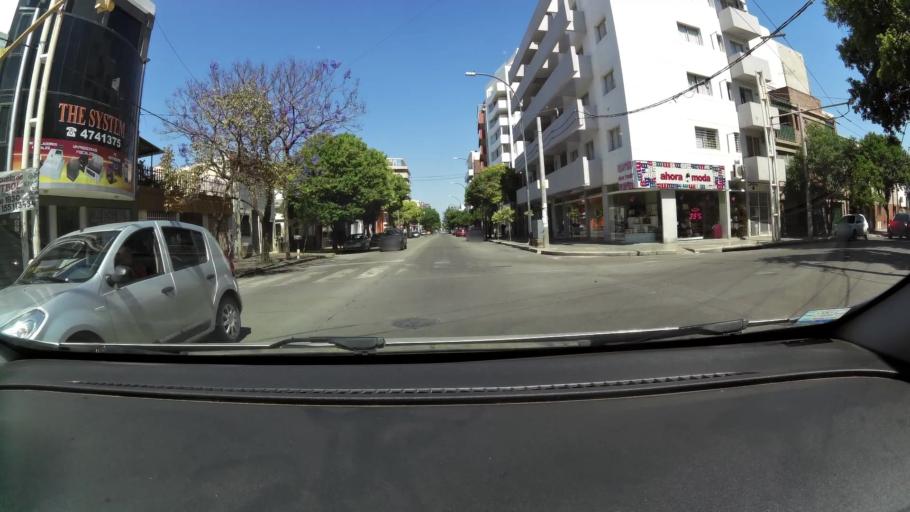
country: AR
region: Cordoba
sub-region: Departamento de Capital
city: Cordoba
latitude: -31.3903
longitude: -64.1850
